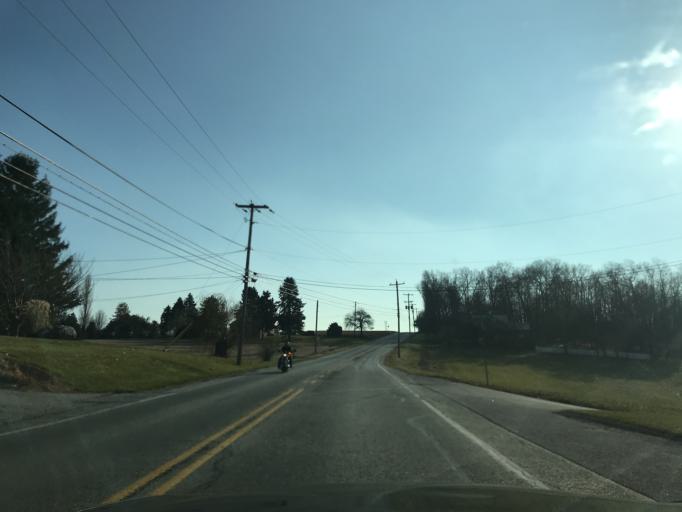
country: US
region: Pennsylvania
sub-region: York County
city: Shrewsbury
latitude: 39.7943
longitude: -76.6785
